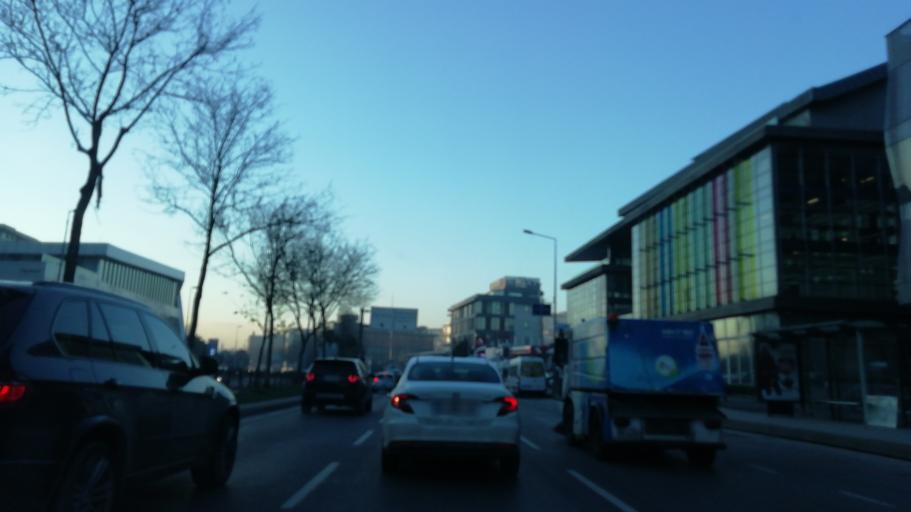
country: TR
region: Istanbul
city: Eminoenue
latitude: 41.0427
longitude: 28.9671
